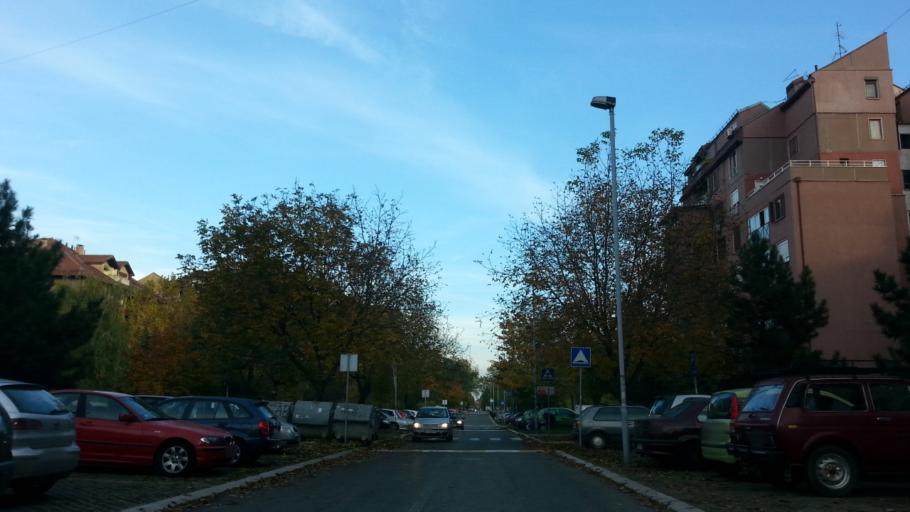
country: RS
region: Central Serbia
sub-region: Belgrade
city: Zemun
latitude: 44.8183
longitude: 20.3741
